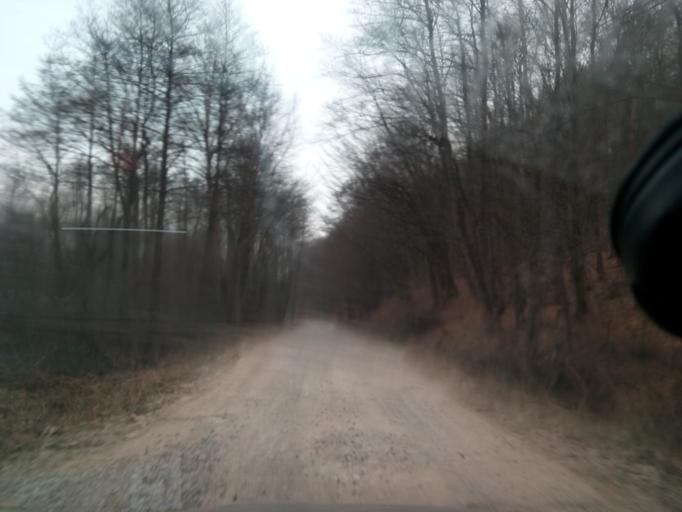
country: SK
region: Kosicky
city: Medzev
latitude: 48.6853
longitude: 20.9057
